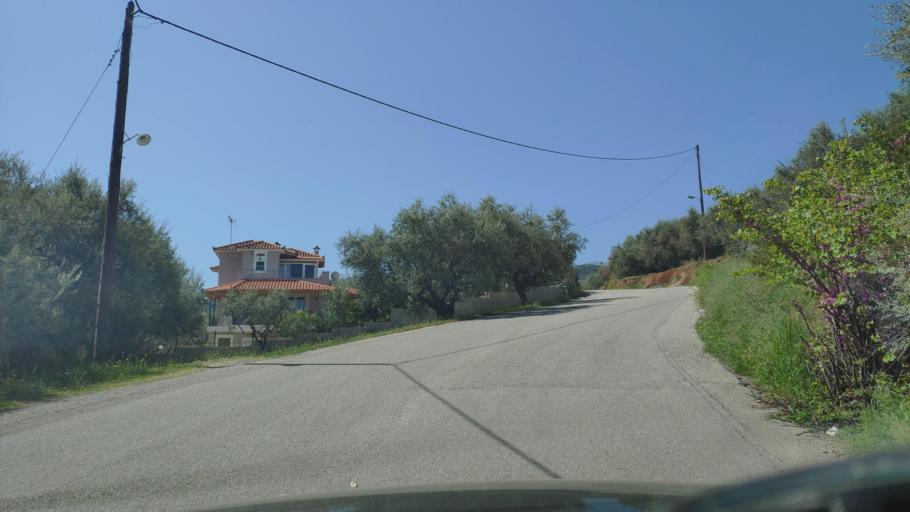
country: GR
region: West Greece
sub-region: Nomos Achaias
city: Aiyira
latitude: 38.1391
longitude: 22.3493
